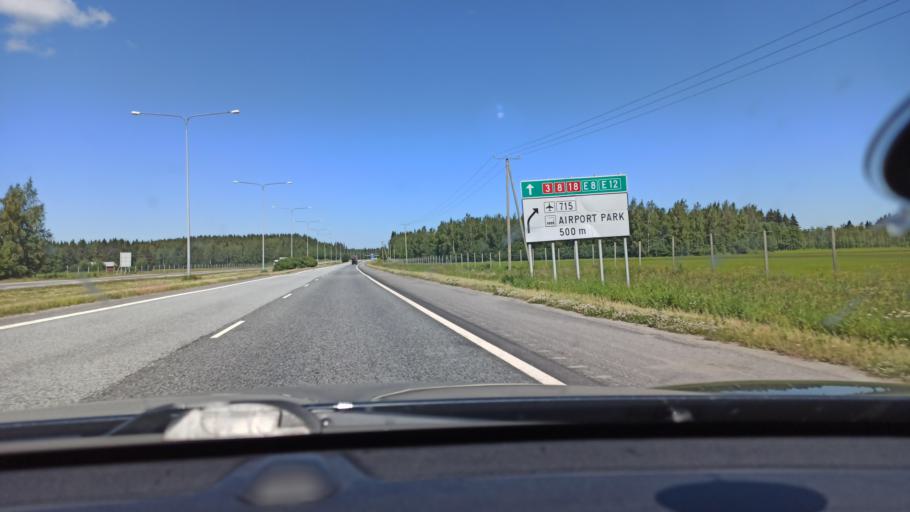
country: FI
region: Ostrobothnia
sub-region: Vaasa
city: Ristinummi
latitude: 63.0453
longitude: 21.7250
